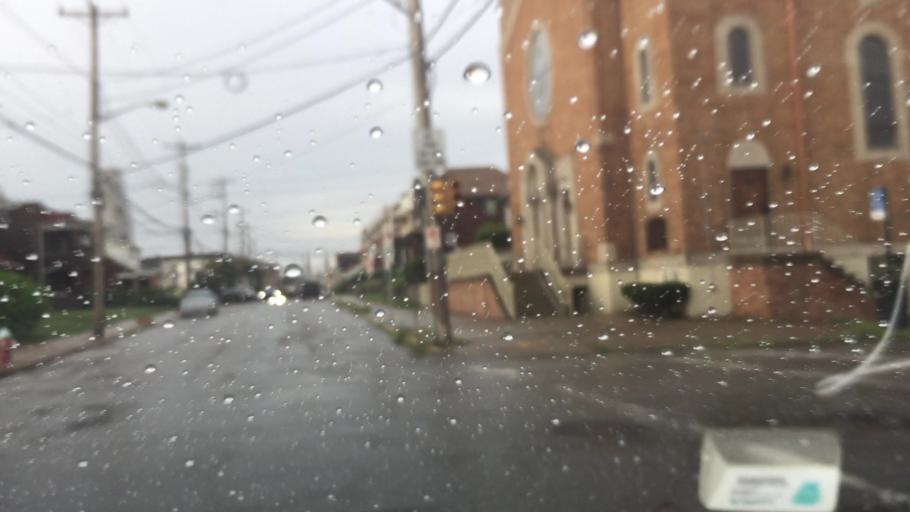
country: US
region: Pennsylvania
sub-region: Allegheny County
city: Bloomfield
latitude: 40.4343
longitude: -79.9532
